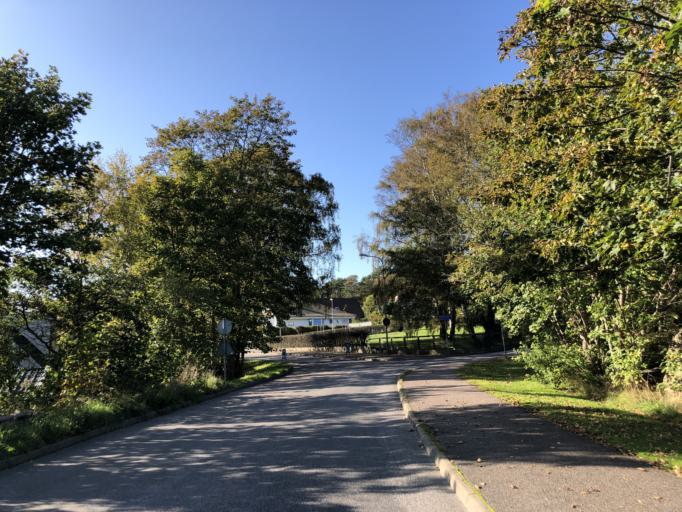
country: SE
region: Vaestra Goetaland
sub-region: Goteborg
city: Billdal
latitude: 57.6200
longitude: 11.8967
